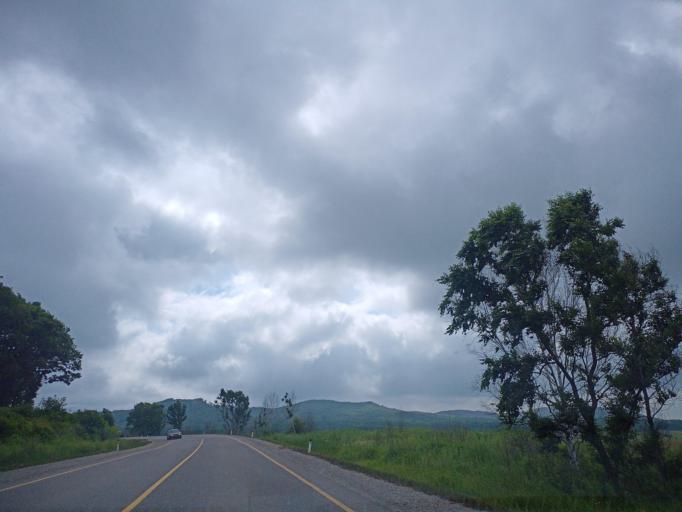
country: RU
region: Primorskiy
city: Dal'nerechensk
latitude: 46.0381
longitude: 133.8850
